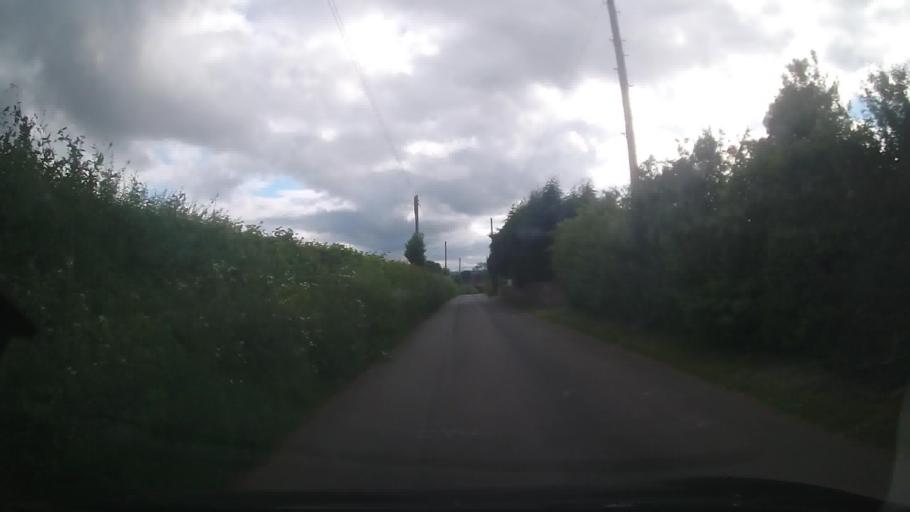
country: GB
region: England
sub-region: Shropshire
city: Stoke upon Tern
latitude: 52.8550
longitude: -2.4887
